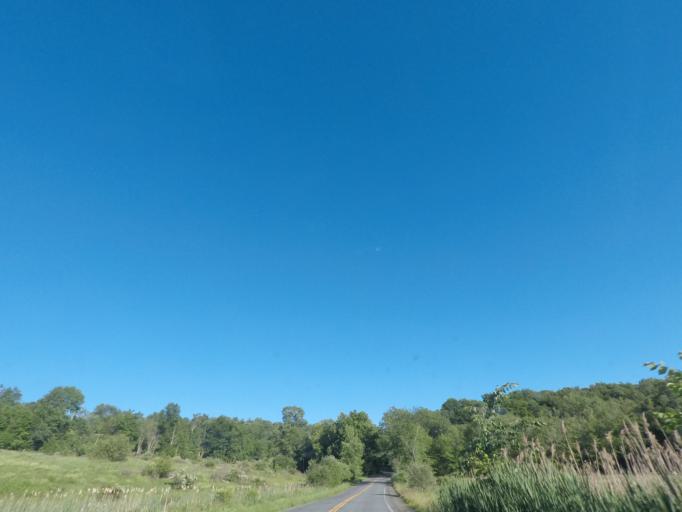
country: US
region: New York
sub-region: Rensselaer County
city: Averill Park
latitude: 42.5759
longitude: -73.5339
